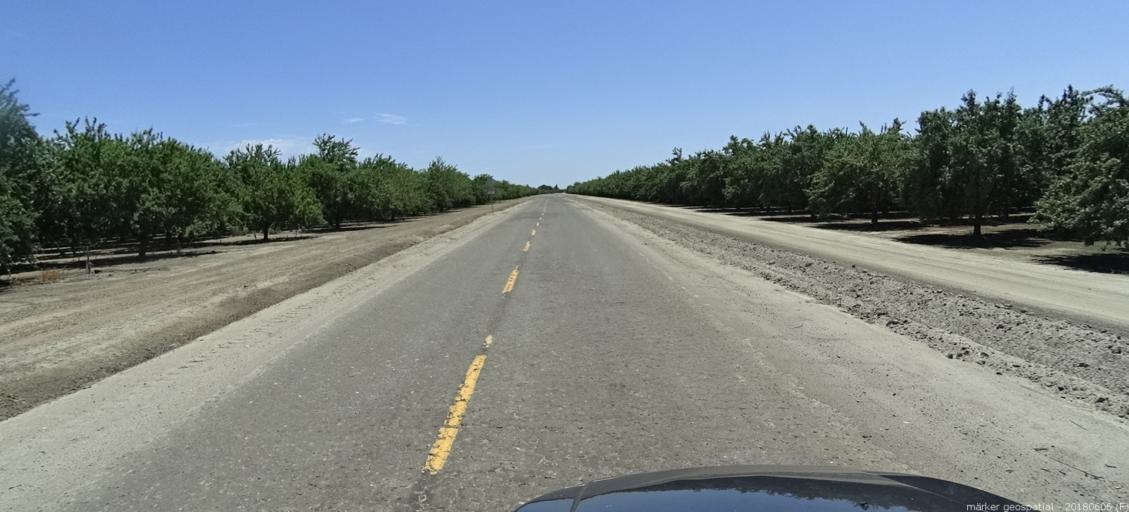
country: US
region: California
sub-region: Fresno County
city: Mendota
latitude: 36.8110
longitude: -120.3646
